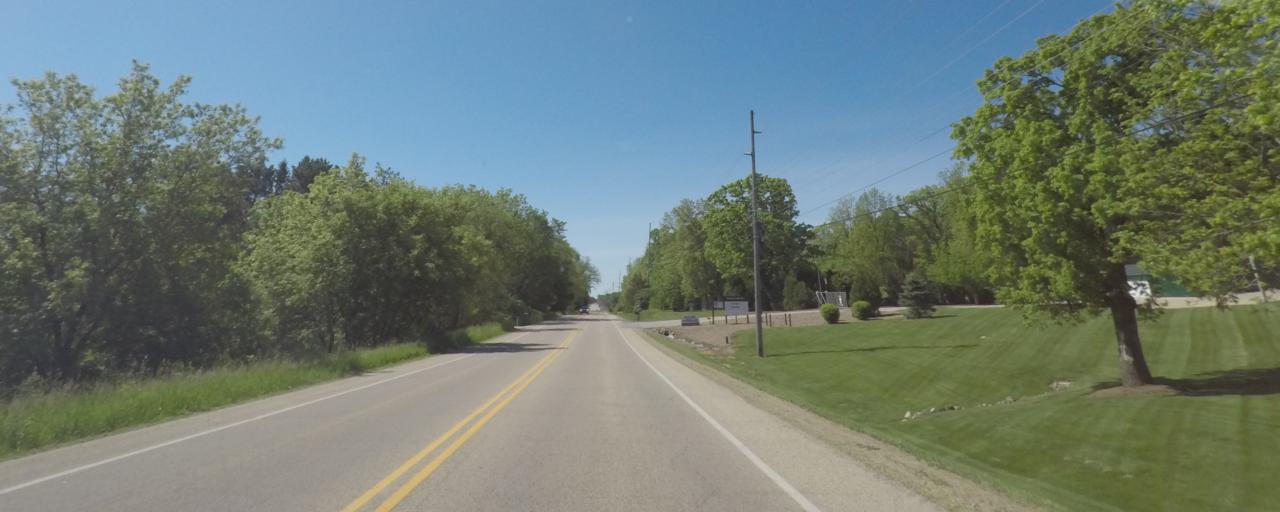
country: US
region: Wisconsin
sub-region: Green County
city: Brooklyn
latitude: 42.8719
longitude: -89.3691
